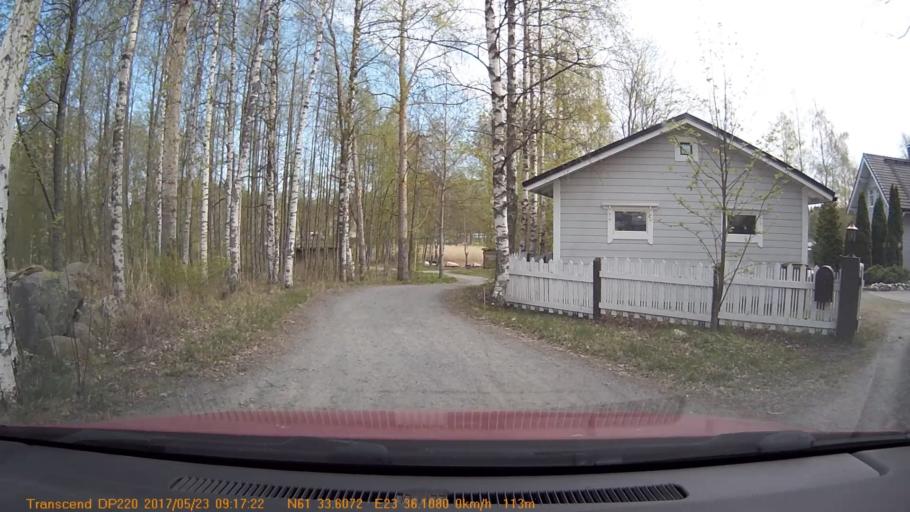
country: FI
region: Pirkanmaa
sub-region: Tampere
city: Yloejaervi
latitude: 61.5601
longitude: 23.6017
